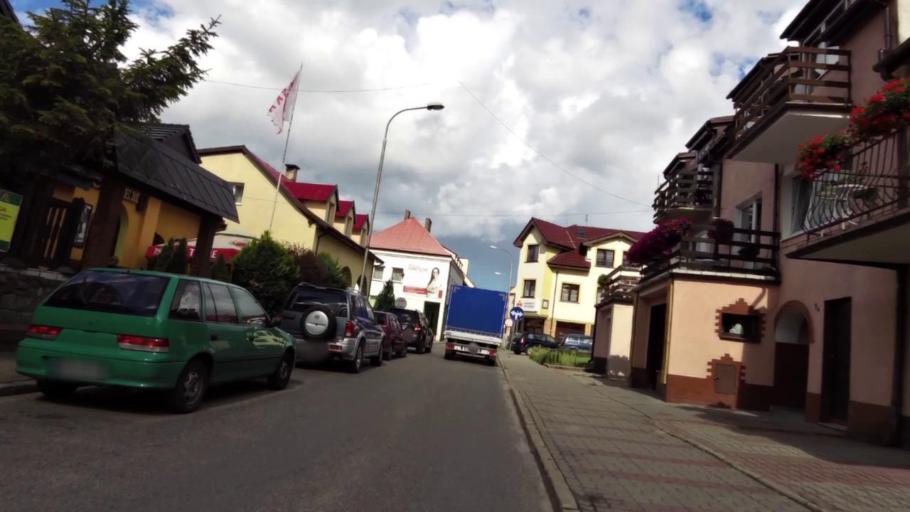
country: PL
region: West Pomeranian Voivodeship
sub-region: Powiat slawienski
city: Darlowo
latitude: 54.4213
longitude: 16.4128
